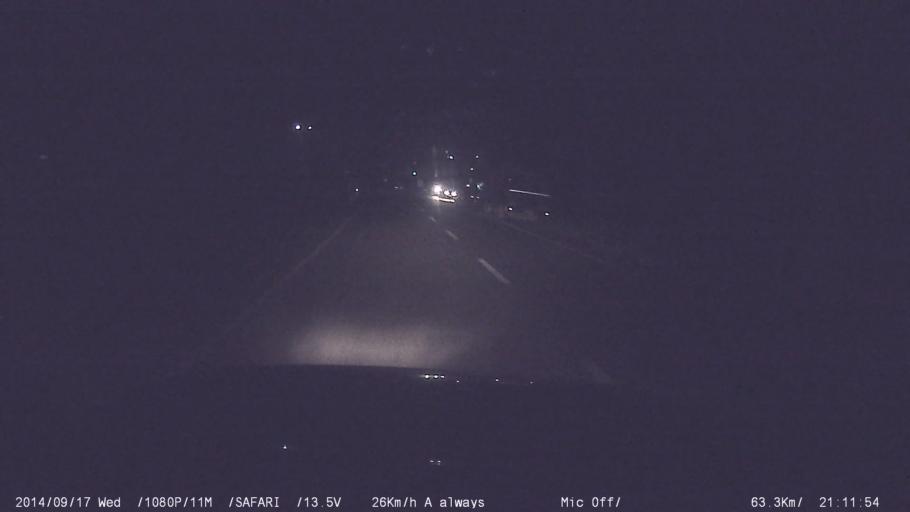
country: IN
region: Kerala
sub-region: Kottayam
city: Changanacheri
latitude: 9.4508
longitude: 76.5456
